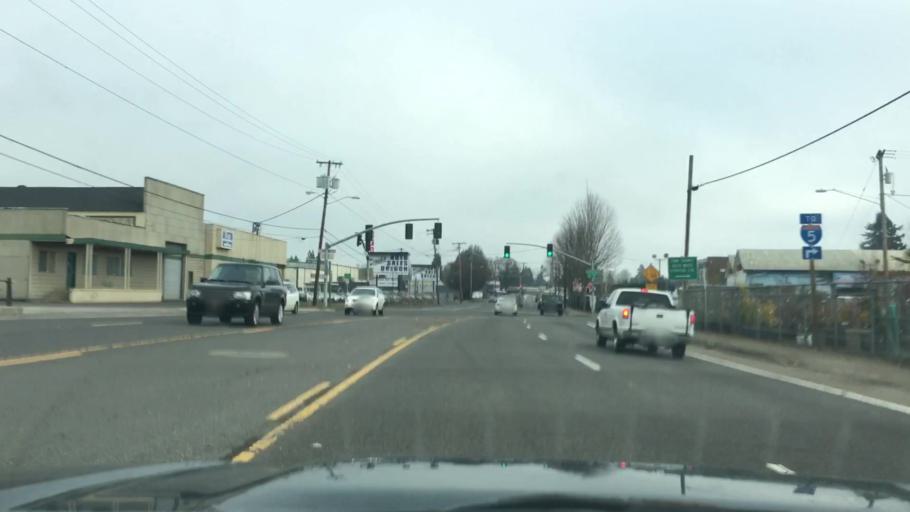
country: US
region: Oregon
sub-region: Lane County
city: Springfield
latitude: 44.0451
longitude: -123.0433
